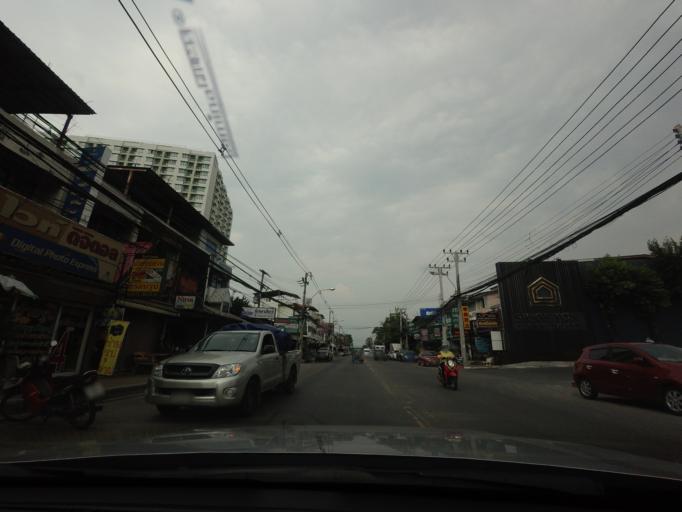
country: TH
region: Chon Buri
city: Phatthaya
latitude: 12.9557
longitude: 100.8909
